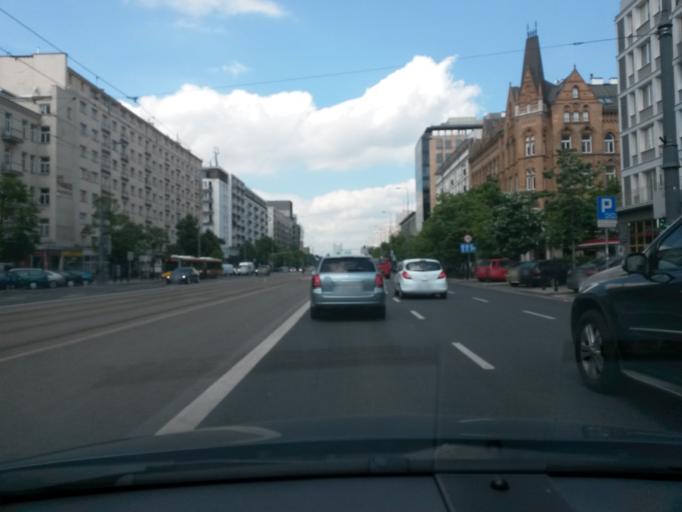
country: PL
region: Masovian Voivodeship
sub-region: Warszawa
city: Srodmiescie
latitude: 52.2250
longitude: 21.0148
